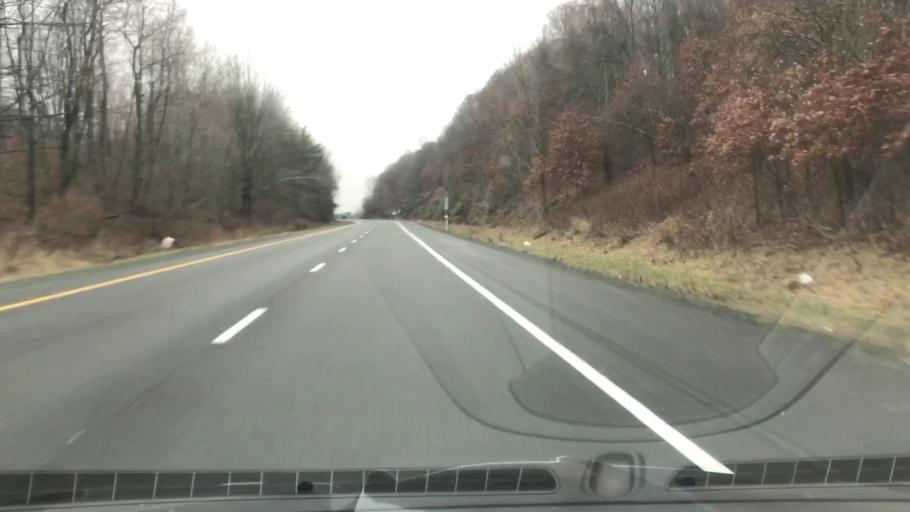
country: US
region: Pennsylvania
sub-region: Pike County
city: Hemlock Farms
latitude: 41.3505
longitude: -75.0137
